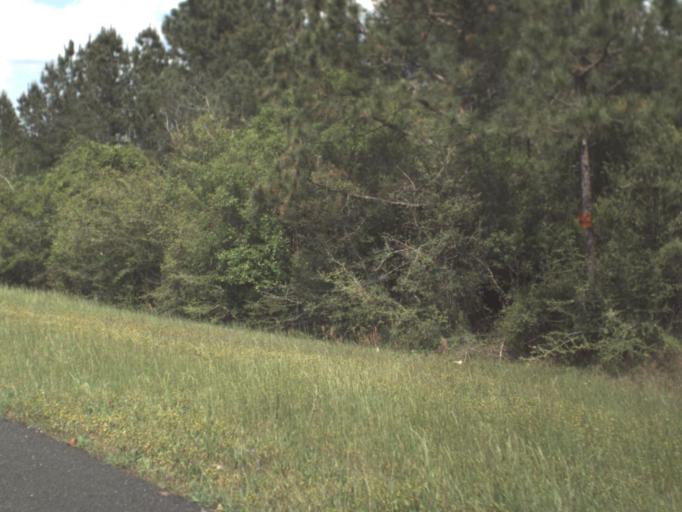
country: US
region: Florida
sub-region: Escambia County
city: Molino
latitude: 30.8110
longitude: -87.3354
